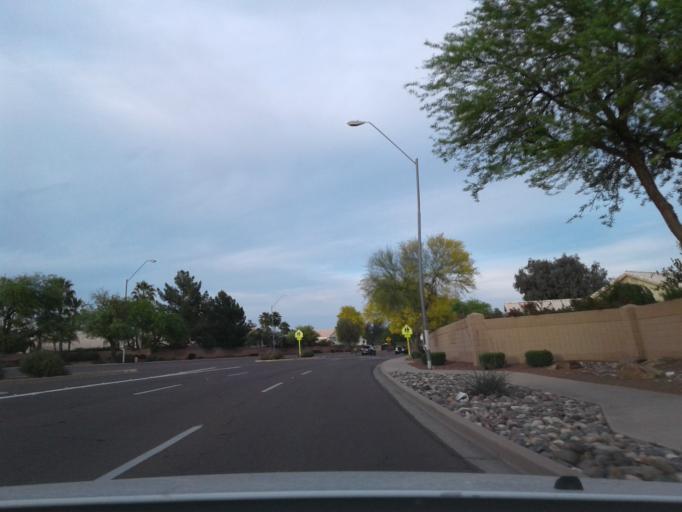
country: US
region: Arizona
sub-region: Maricopa County
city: Glendale
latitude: 33.6321
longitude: -112.0856
